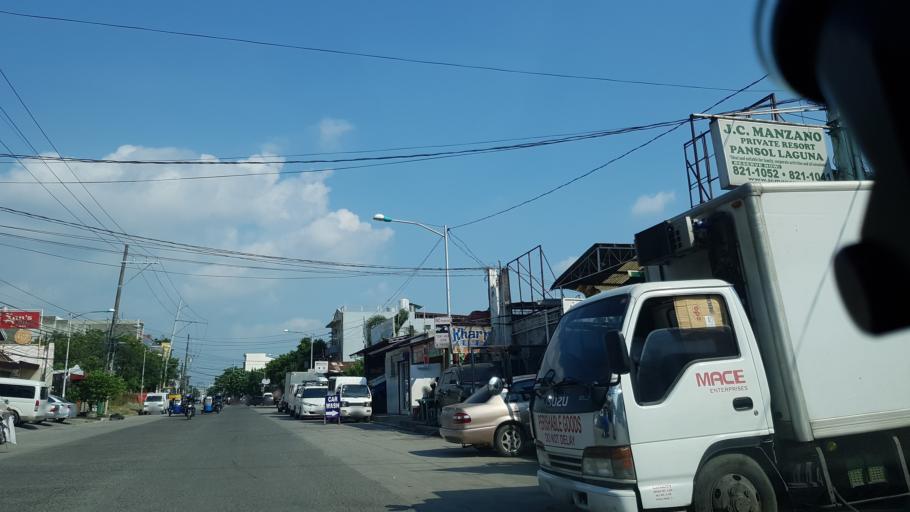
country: PH
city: Sambayanihan People's Village
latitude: 14.4890
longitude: 121.0205
